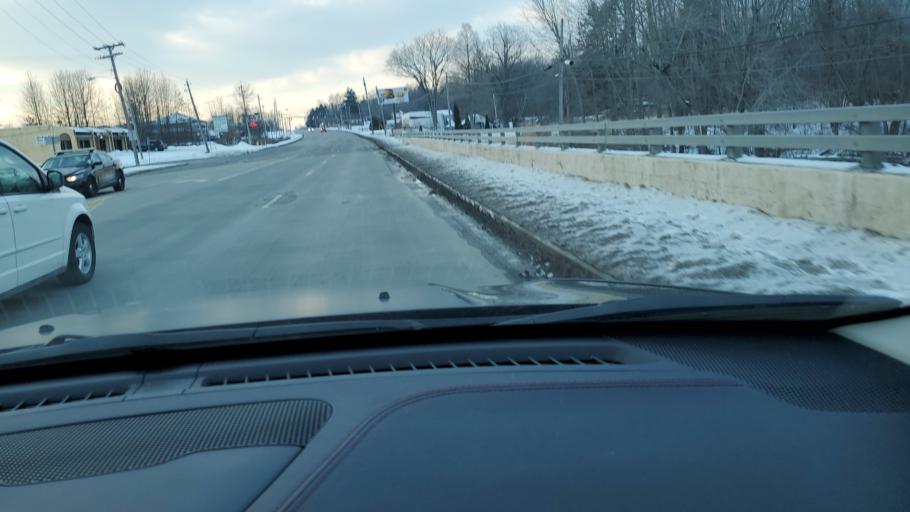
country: US
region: Ohio
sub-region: Trumbull County
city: Leavittsburg
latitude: 41.2577
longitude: -80.8648
